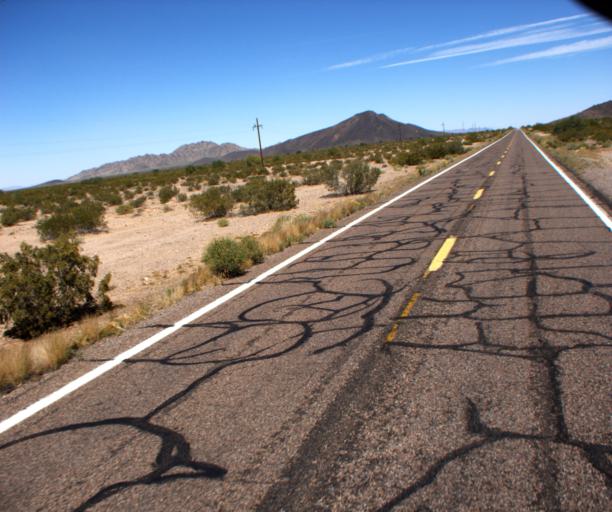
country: US
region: Arizona
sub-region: Maricopa County
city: Gila Bend
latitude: 32.7307
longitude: -112.8352
